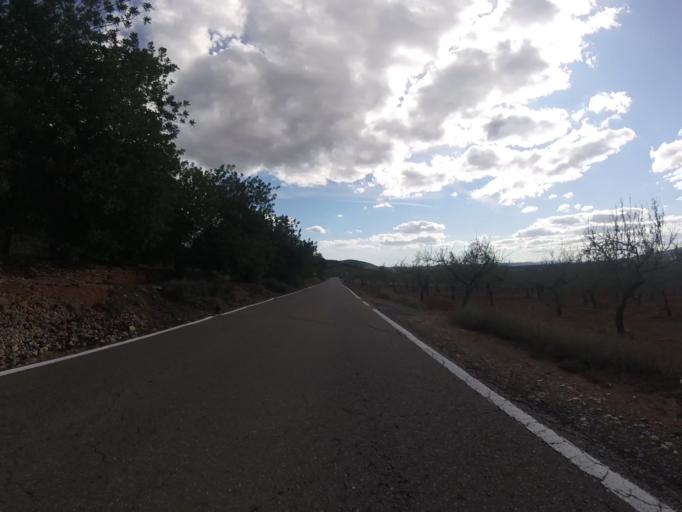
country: ES
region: Valencia
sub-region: Provincia de Castello
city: Cuevas de Vinroma
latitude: 40.3615
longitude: 0.1242
